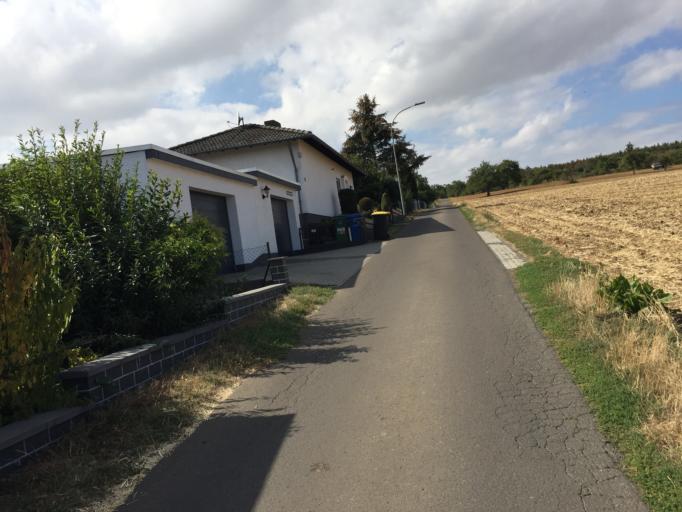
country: DE
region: Hesse
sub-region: Regierungsbezirk Darmstadt
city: Wolfersheim
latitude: 50.4544
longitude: 8.8347
